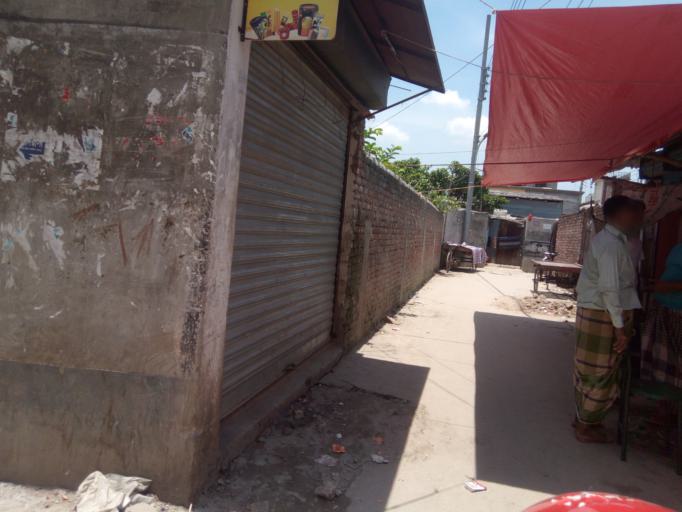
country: BD
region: Dhaka
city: Paltan
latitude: 23.7561
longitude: 90.4339
